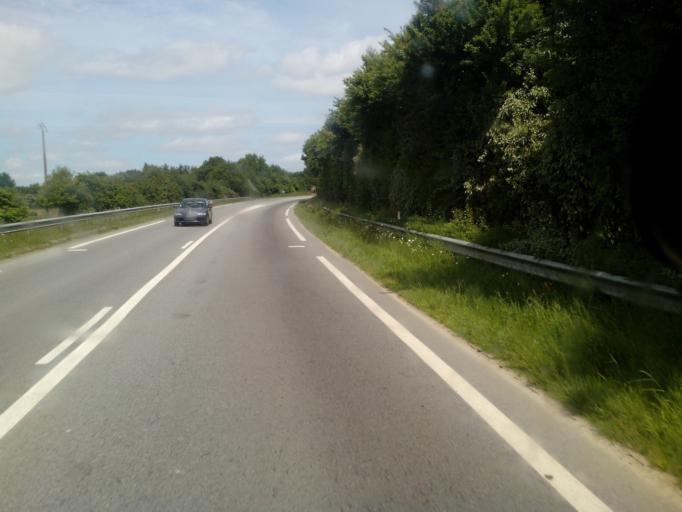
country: FR
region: Brittany
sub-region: Departement d'Ille-et-Vilaine
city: Chevaigne
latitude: 48.2445
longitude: -1.6209
